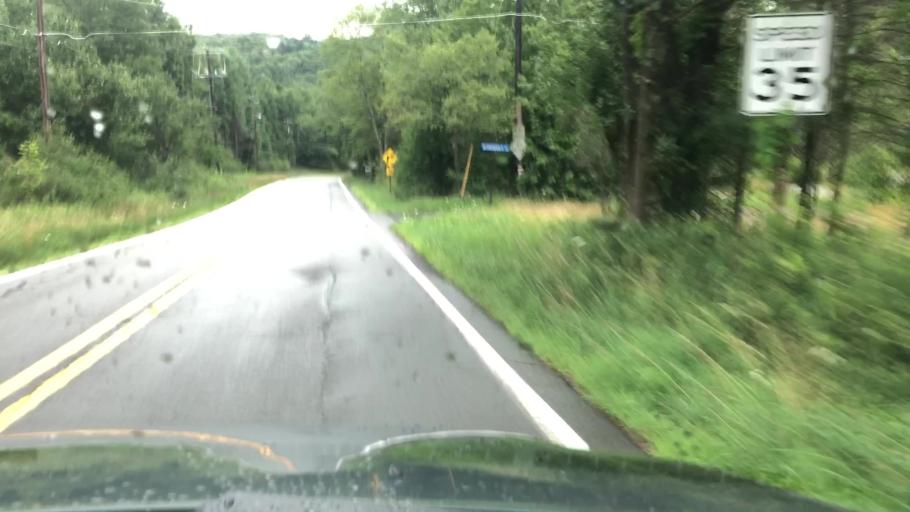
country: US
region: Pennsylvania
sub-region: Monroe County
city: Mountainhome
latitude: 41.2845
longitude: -75.2496
